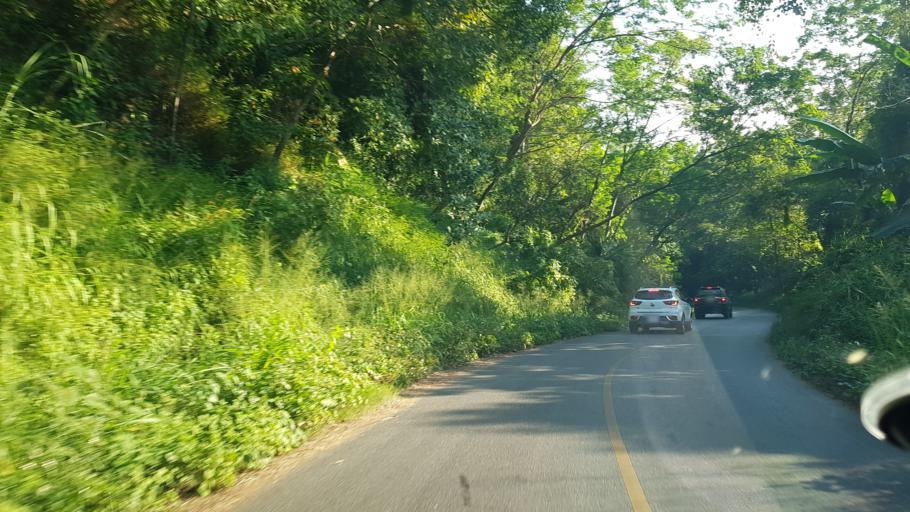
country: TH
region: Chiang Rai
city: Mae Fa Luang
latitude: 20.3164
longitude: 99.8178
